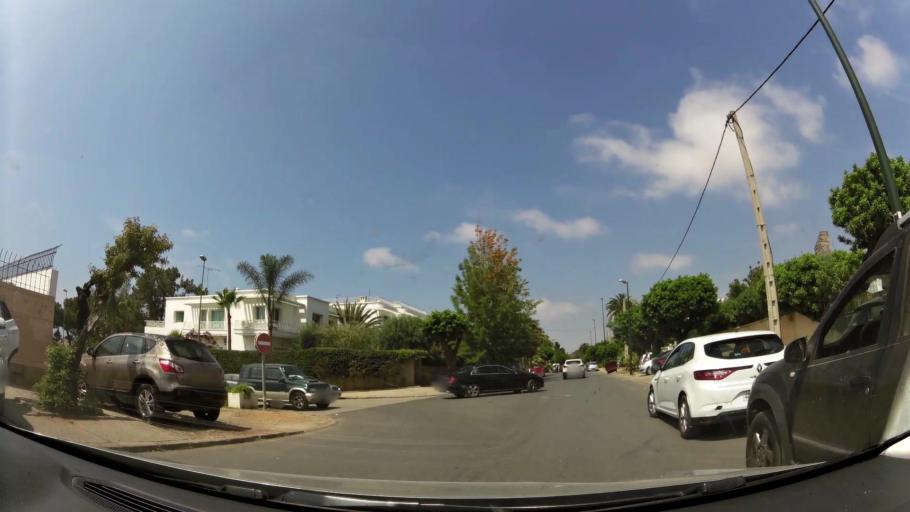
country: MA
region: Rabat-Sale-Zemmour-Zaer
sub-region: Rabat
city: Rabat
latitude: 33.9906
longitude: -6.8451
